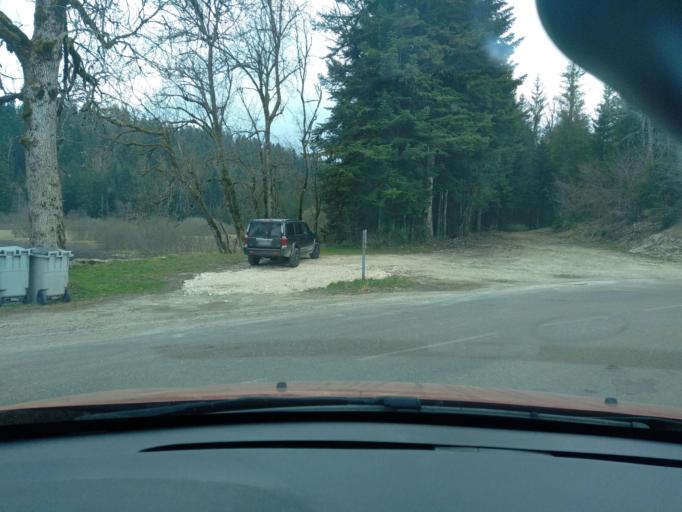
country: FR
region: Franche-Comte
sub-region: Departement du Jura
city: Moirans-en-Montagne
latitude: 46.4552
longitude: 5.7615
